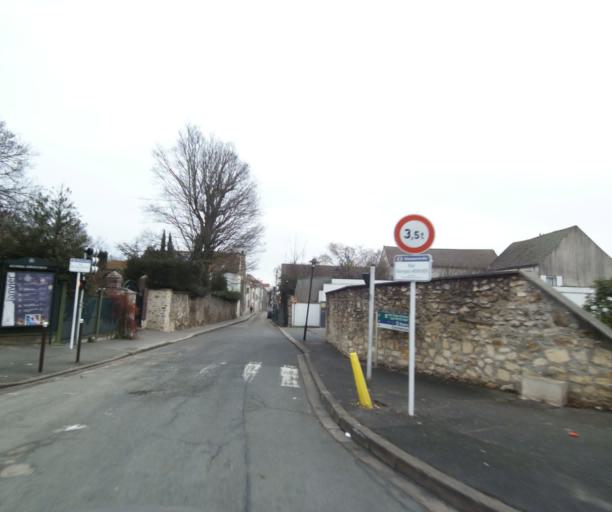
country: FR
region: Ile-de-France
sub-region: Departement du Val-de-Marne
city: Villeneuve-le-Roi
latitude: 48.7337
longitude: 2.4059
